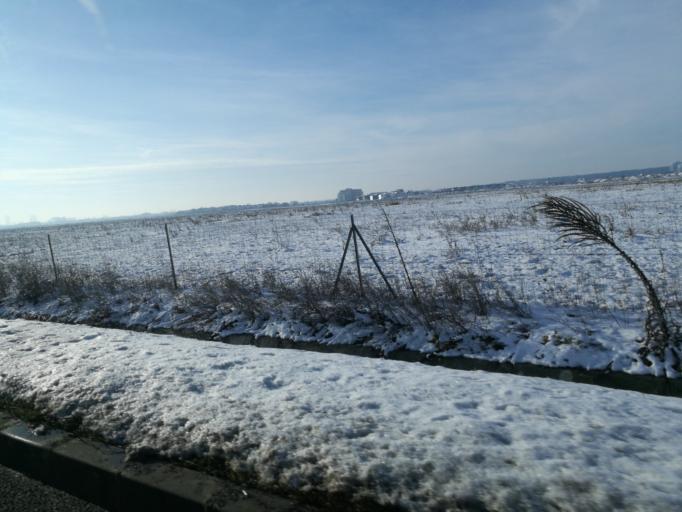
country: RO
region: Ilfov
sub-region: Voluntari City
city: Voluntari
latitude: 44.5145
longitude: 26.1672
